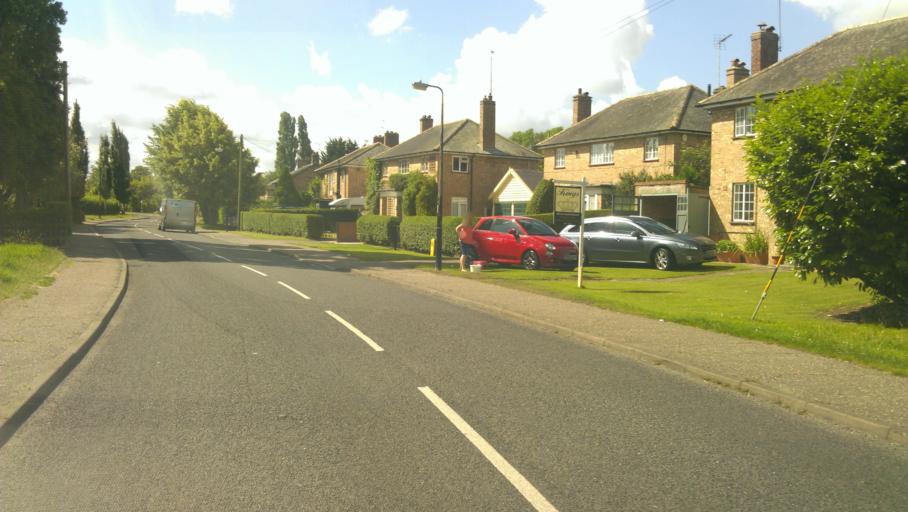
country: GB
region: England
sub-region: Essex
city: Rayne
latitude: 51.8487
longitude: 0.6262
